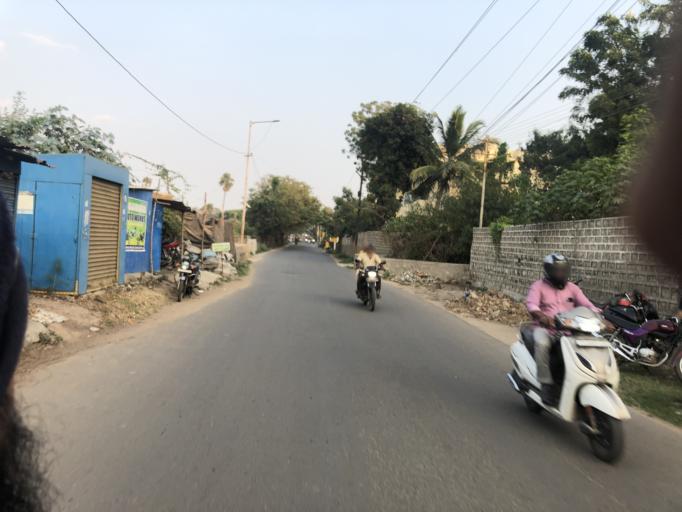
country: IN
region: Telangana
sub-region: Rangareddi
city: Kukatpalli
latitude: 17.4627
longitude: 78.4348
